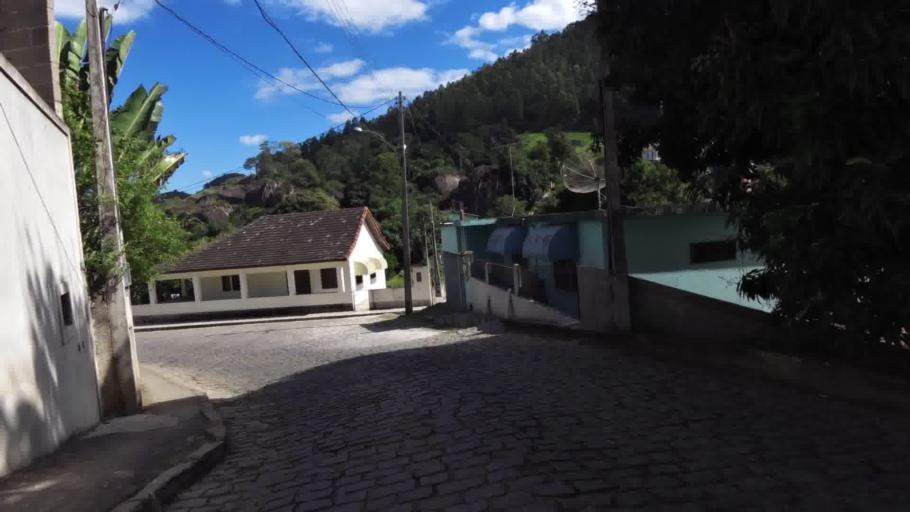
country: BR
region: Espirito Santo
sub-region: Rio Novo Do Sul
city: Rio Novo do Sul
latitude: -20.8652
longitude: -40.9382
